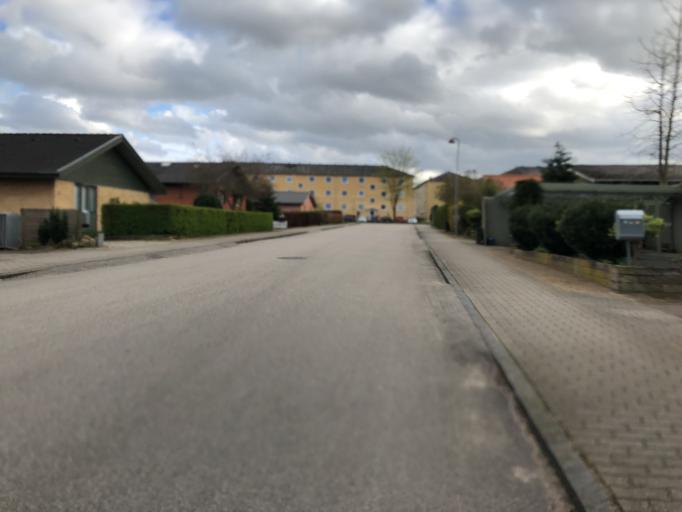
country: DK
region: Zealand
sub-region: Ringsted Kommune
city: Ringsted
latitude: 55.4453
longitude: 11.8060
